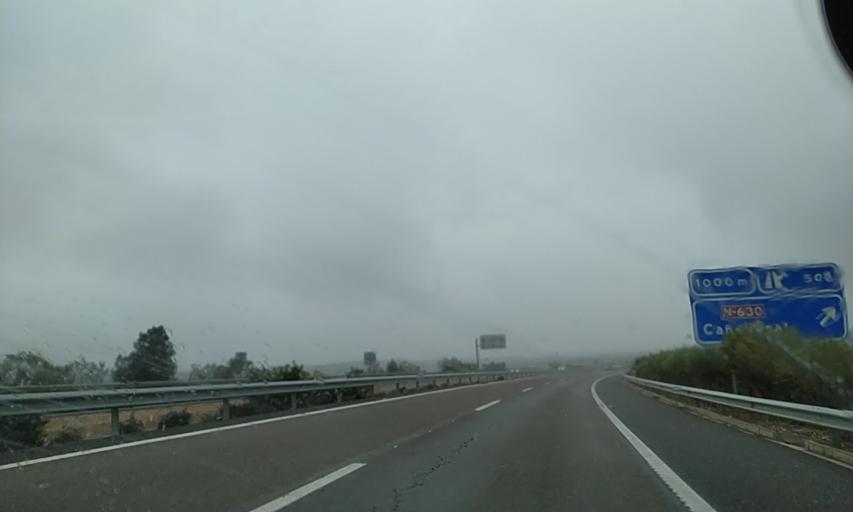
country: ES
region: Extremadura
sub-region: Provincia de Caceres
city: Casas de Millan
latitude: 39.8115
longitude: -6.3629
